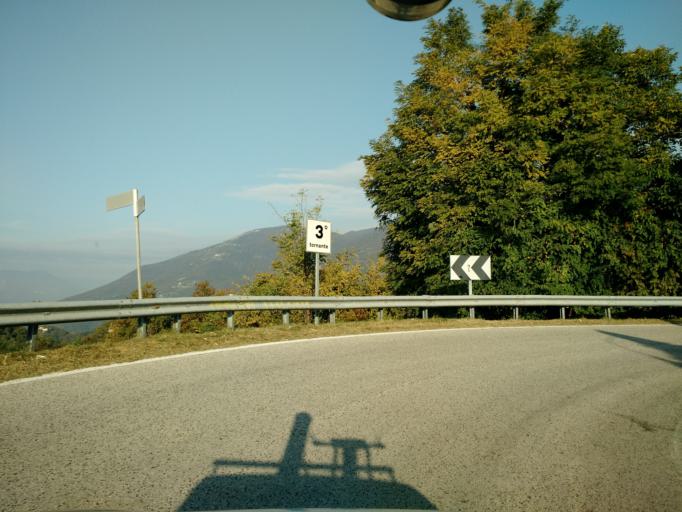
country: IT
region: Veneto
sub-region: Provincia di Vicenza
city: Salcedo
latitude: 45.7643
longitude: 11.5661
